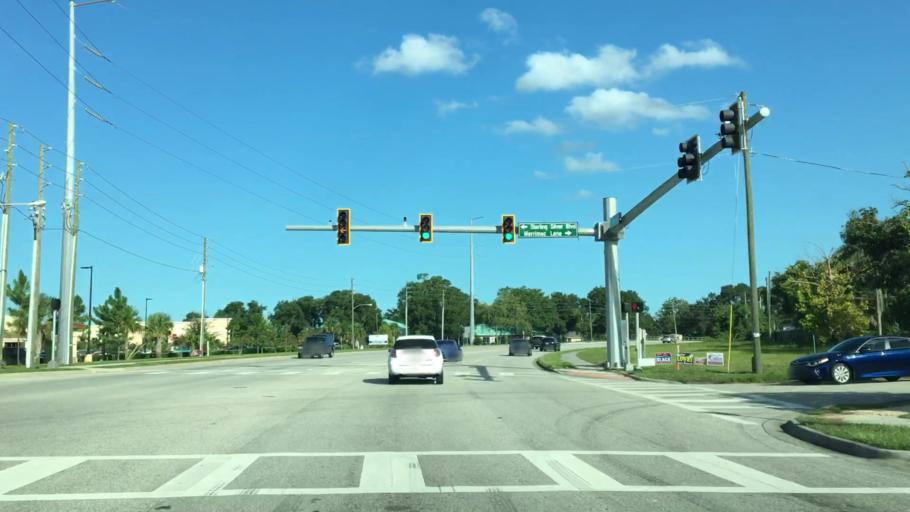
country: US
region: Florida
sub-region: Volusia County
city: Deltona
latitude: 28.9071
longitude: -81.2476
